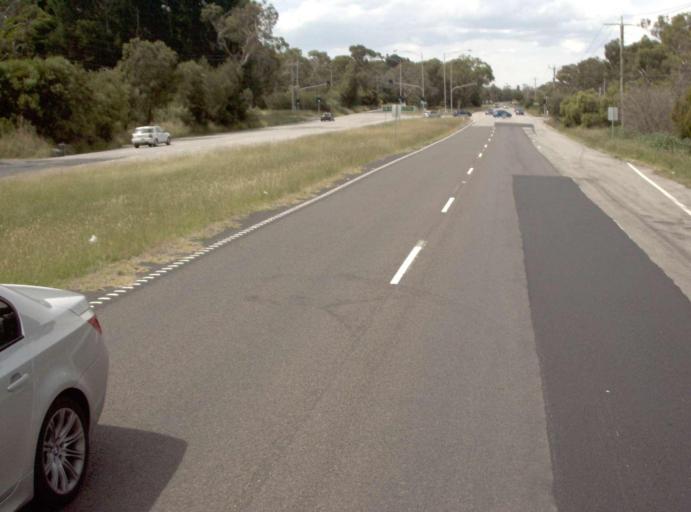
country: AU
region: Victoria
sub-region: Mornington Peninsula
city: Baxter
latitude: -38.1969
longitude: 145.1325
